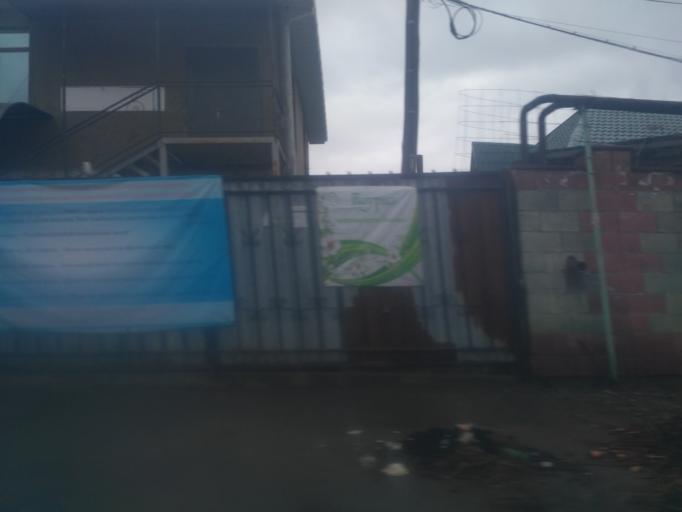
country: KZ
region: Almaty Oblysy
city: Burunday
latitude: 43.2205
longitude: 76.7449
